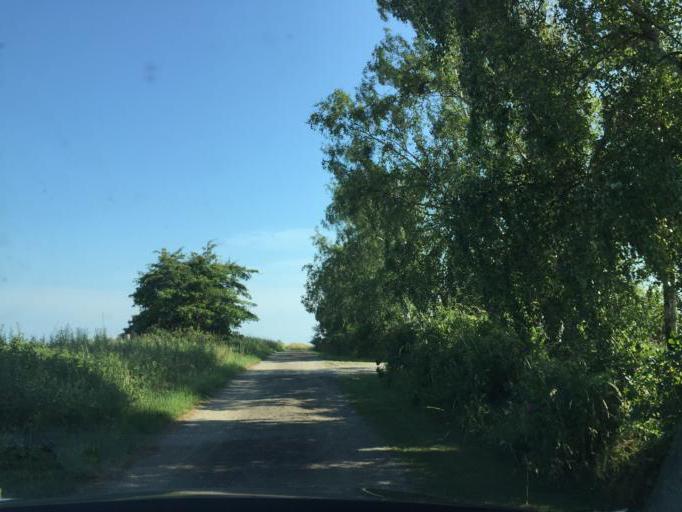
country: DK
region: Zealand
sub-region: Slagelse Kommune
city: Korsor
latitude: 55.2187
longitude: 11.1767
